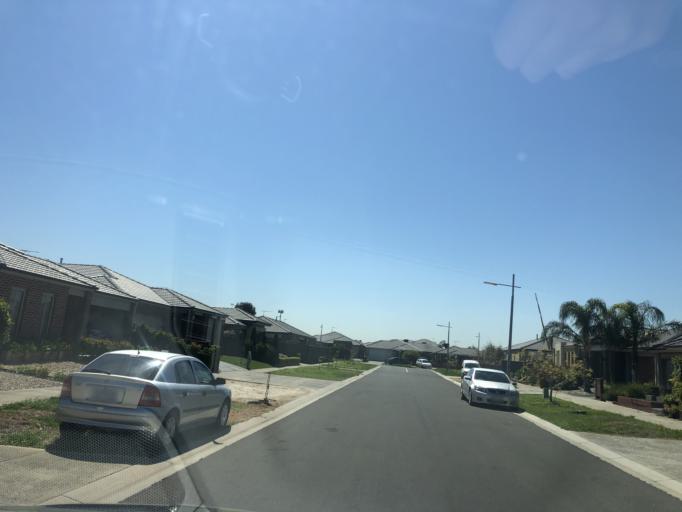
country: AU
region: Victoria
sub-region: Wyndham
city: Point Cook
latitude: -37.9042
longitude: 144.7314
